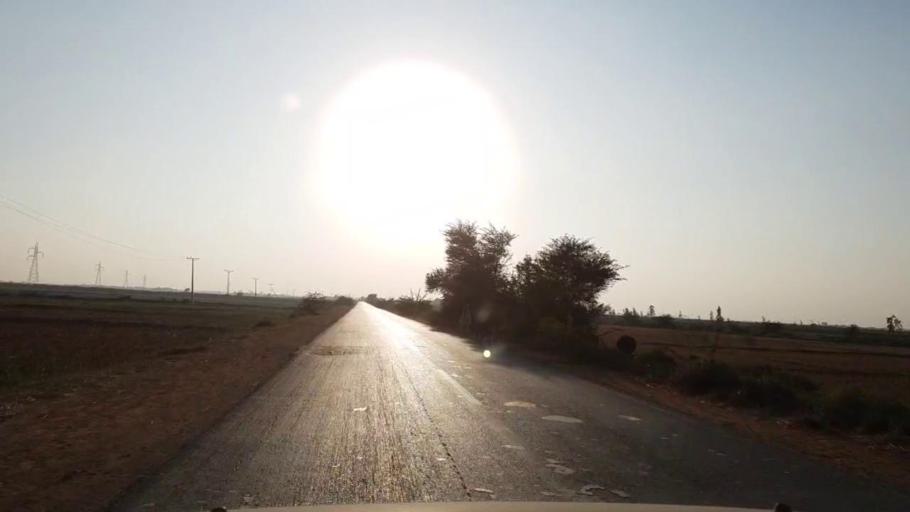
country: PK
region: Sindh
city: Daro Mehar
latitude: 24.6396
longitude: 68.1159
